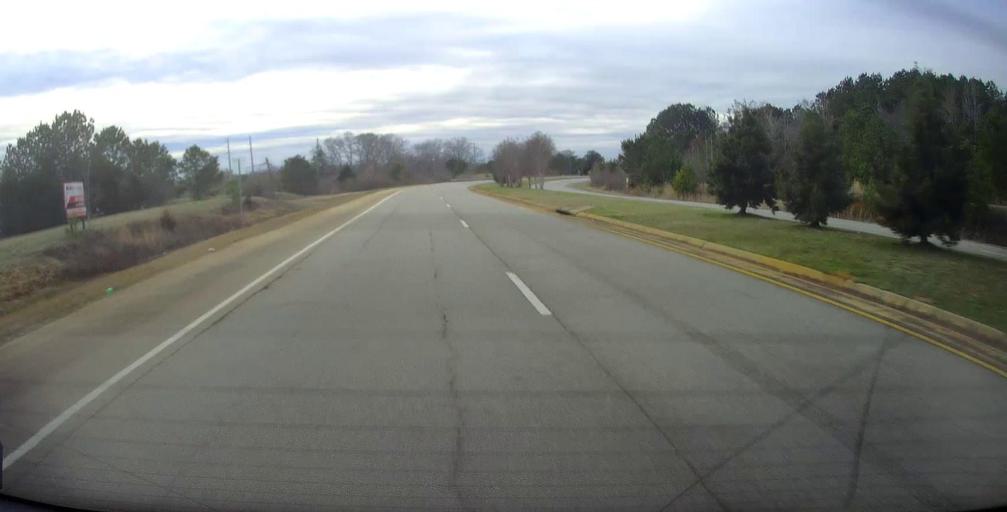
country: US
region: Georgia
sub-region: Troup County
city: West Point
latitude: 32.9315
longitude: -85.1235
